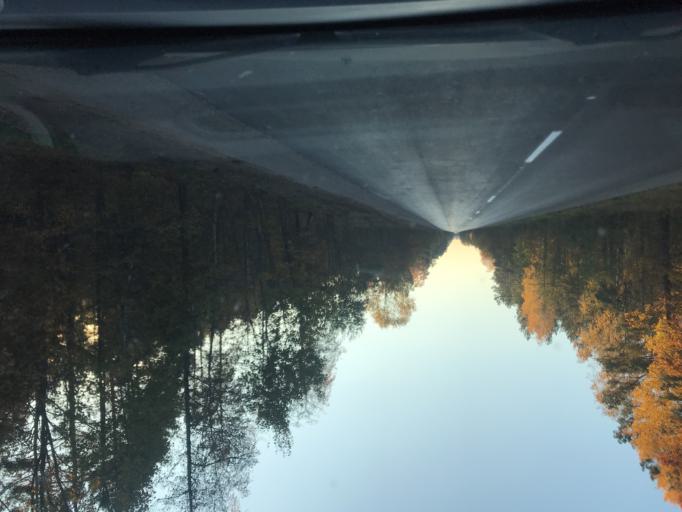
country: BY
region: Gomel
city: Brahin
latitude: 51.8742
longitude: 30.3833
